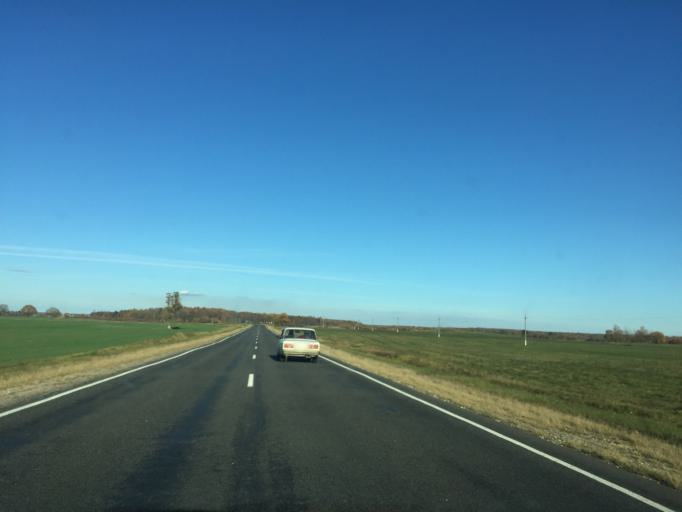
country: BY
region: Vitebsk
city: Dzisna
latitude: 55.3118
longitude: 28.2654
